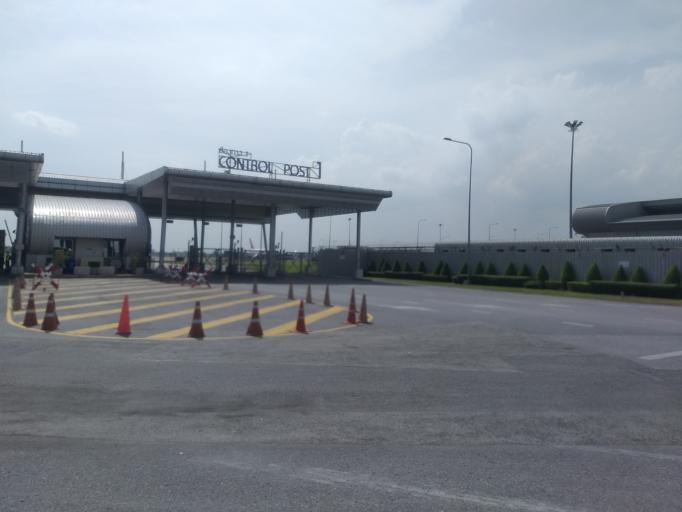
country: TH
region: Bangkok
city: Lat Krabang
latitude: 13.6971
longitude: 100.7487
